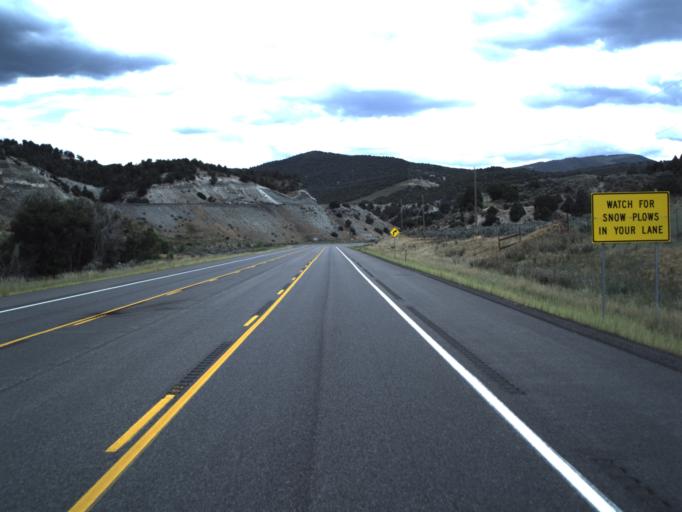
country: US
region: Utah
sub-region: Sanpete County
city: Fairview
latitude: 39.9474
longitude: -111.2119
